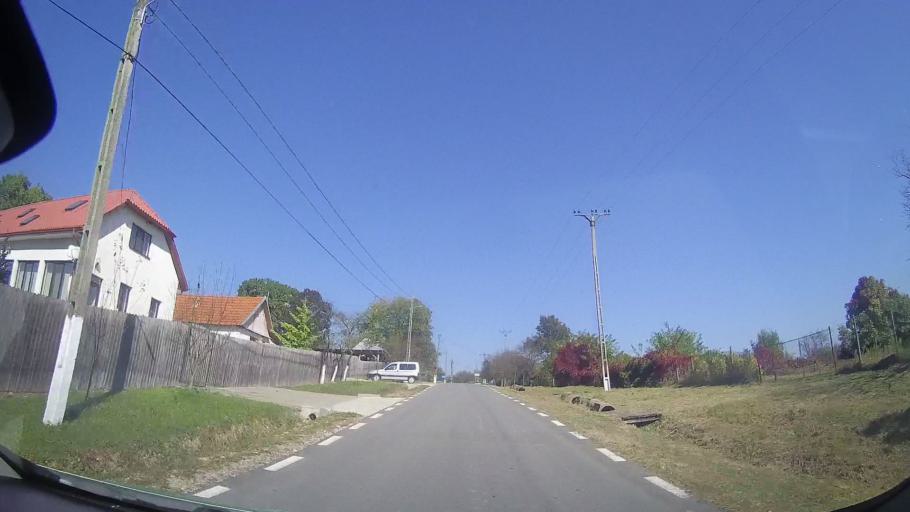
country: RO
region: Timis
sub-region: Comuna Ohaba Lunga
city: Ohaba Lunga
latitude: 45.9058
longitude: 21.9369
